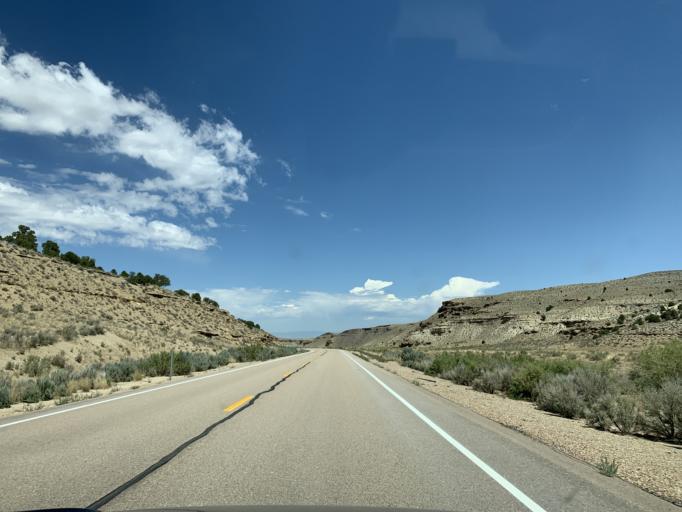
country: US
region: Utah
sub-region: Duchesne County
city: Duchesne
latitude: 39.9950
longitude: -110.1546
